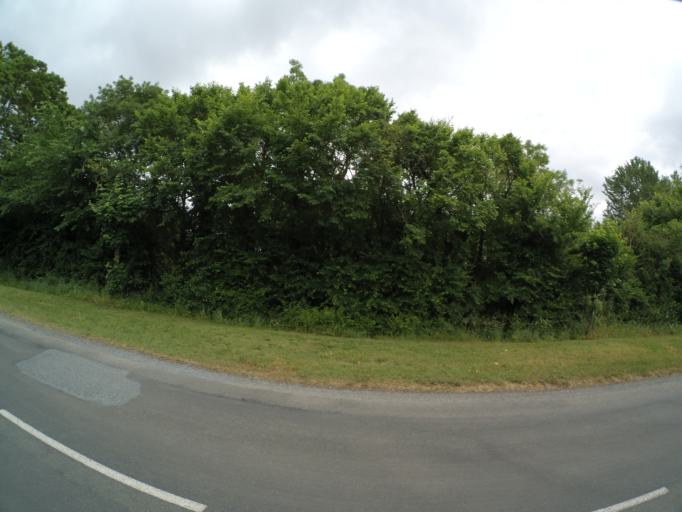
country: FR
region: Poitou-Charentes
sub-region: Departement de la Charente-Maritime
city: Saint-Laurent-de-la-Pree
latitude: 45.9839
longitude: -1.0064
